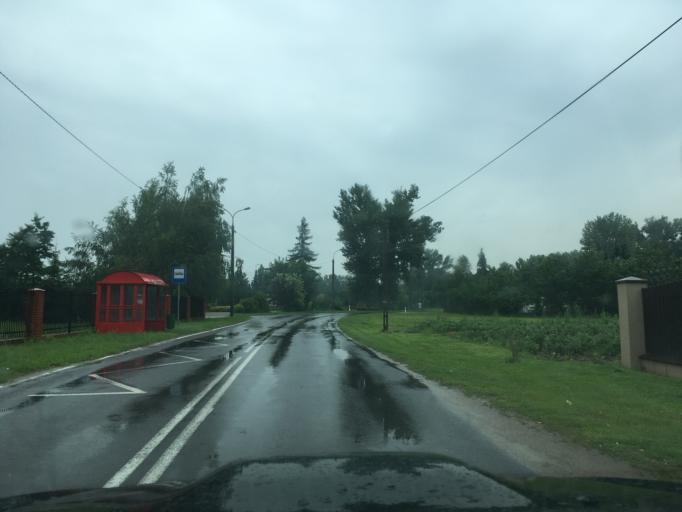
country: PL
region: Masovian Voivodeship
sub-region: Powiat piaseczynski
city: Gora Kalwaria
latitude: 51.9927
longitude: 21.2417
